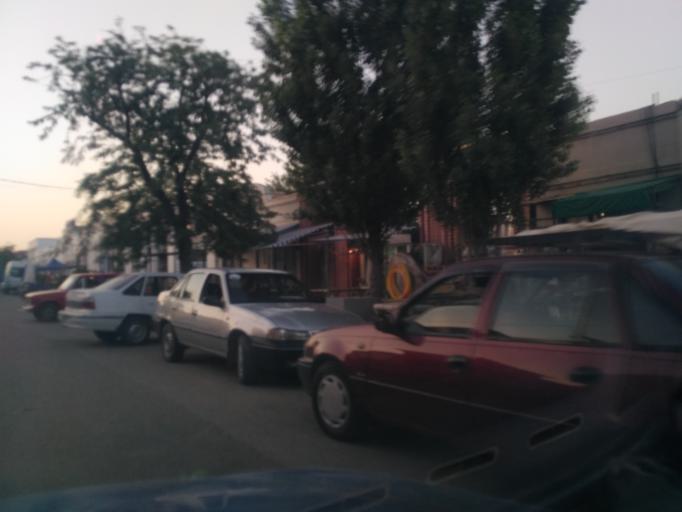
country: UZ
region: Sirdaryo
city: Guliston
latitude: 40.4924
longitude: 68.7671
